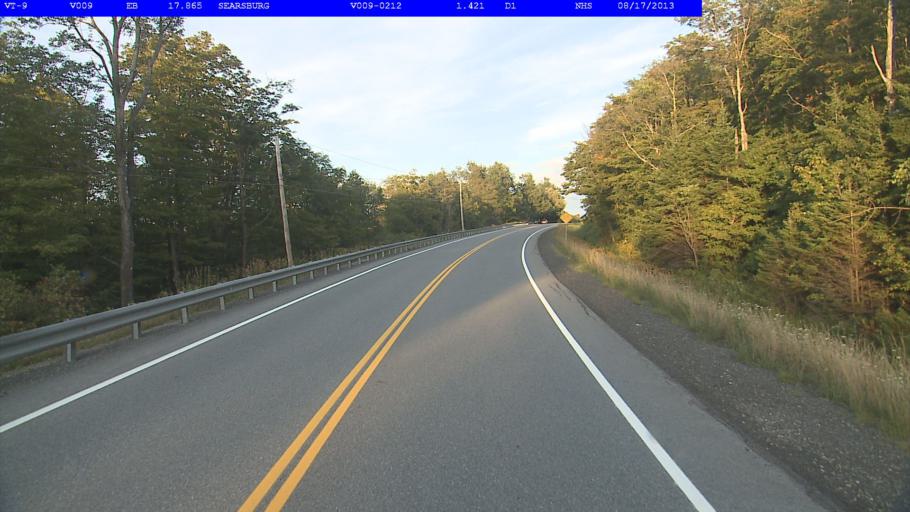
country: US
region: Vermont
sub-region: Windham County
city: Dover
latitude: 42.8954
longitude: -72.9844
